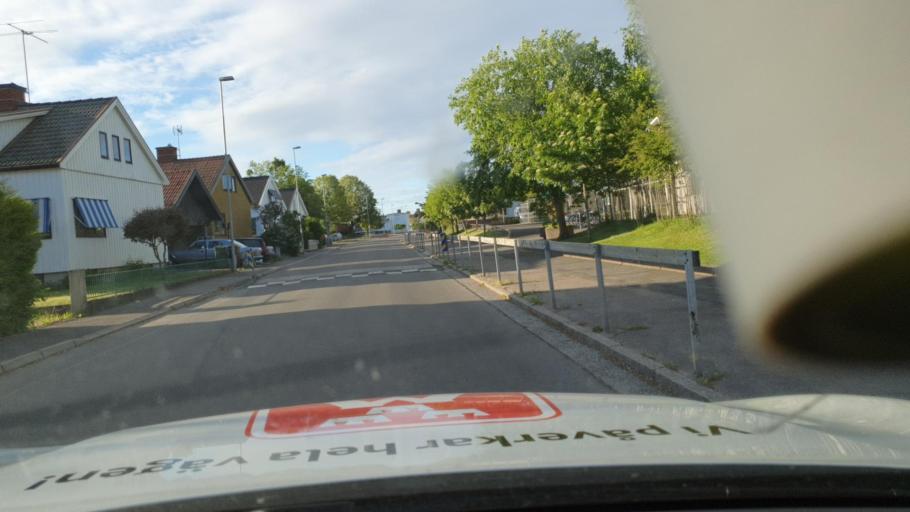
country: SE
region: Vaestra Goetaland
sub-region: Falkopings Kommun
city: Falkoeping
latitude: 58.1652
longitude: 13.5602
